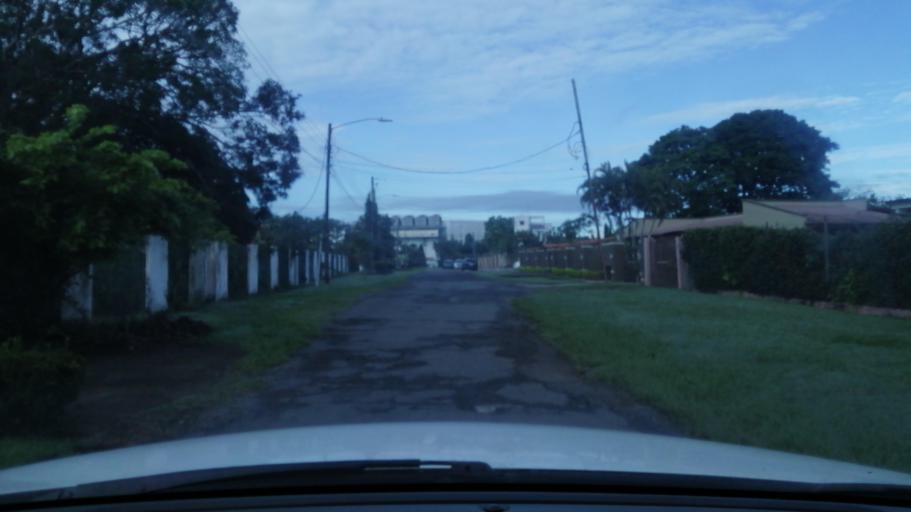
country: PA
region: Chiriqui
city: Mata del Nance
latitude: 8.4481
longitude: -82.4184
